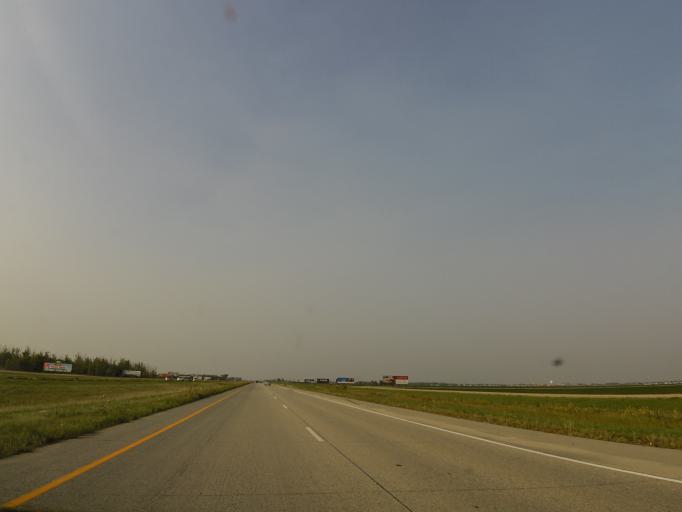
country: US
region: North Dakota
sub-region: Cass County
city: Horace
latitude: 46.7581
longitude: -96.8395
